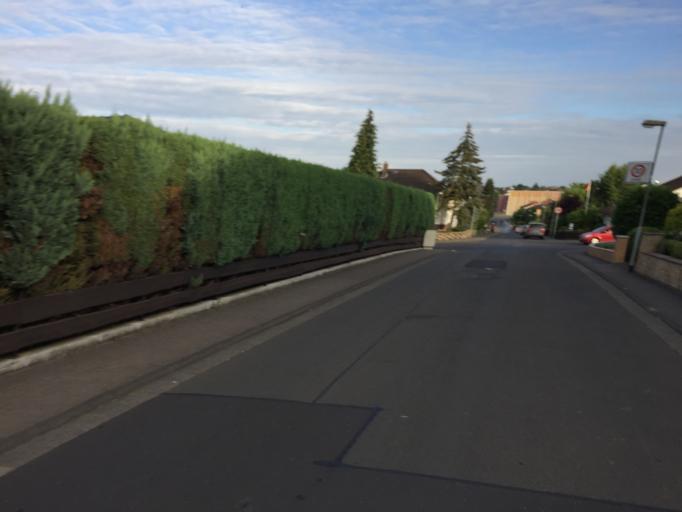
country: DE
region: Hesse
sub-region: Regierungsbezirk Giessen
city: Reiskirchen
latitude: 50.6014
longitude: 8.8249
